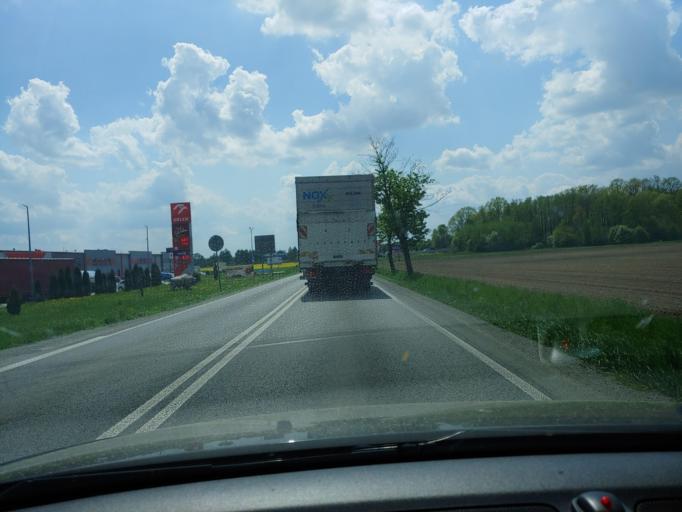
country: PL
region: Lesser Poland Voivodeship
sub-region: Powiat tarnowski
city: Lisia Gora
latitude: 50.0750
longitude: 21.0209
